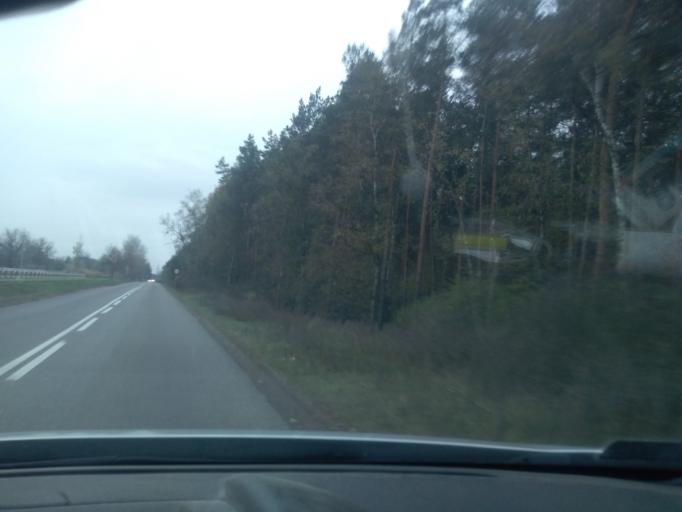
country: PL
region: Greater Poland Voivodeship
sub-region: Powiat poznanski
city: Murowana Goslina
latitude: 52.5558
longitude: 16.9747
